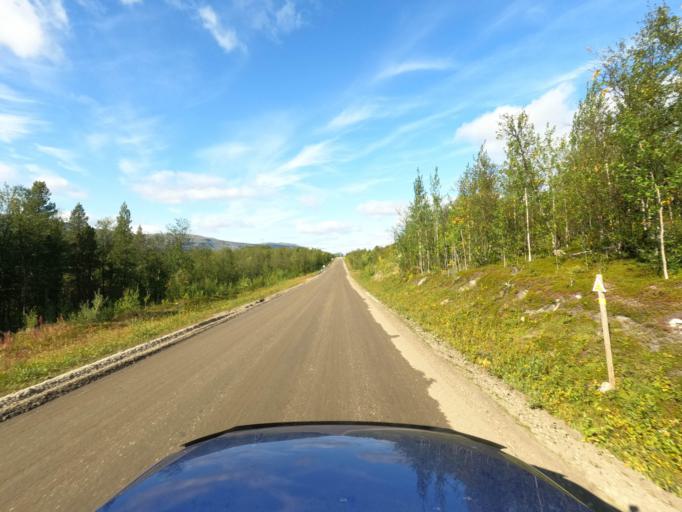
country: NO
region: Finnmark Fylke
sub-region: Porsanger
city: Lakselv
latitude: 69.8763
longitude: 25.0293
